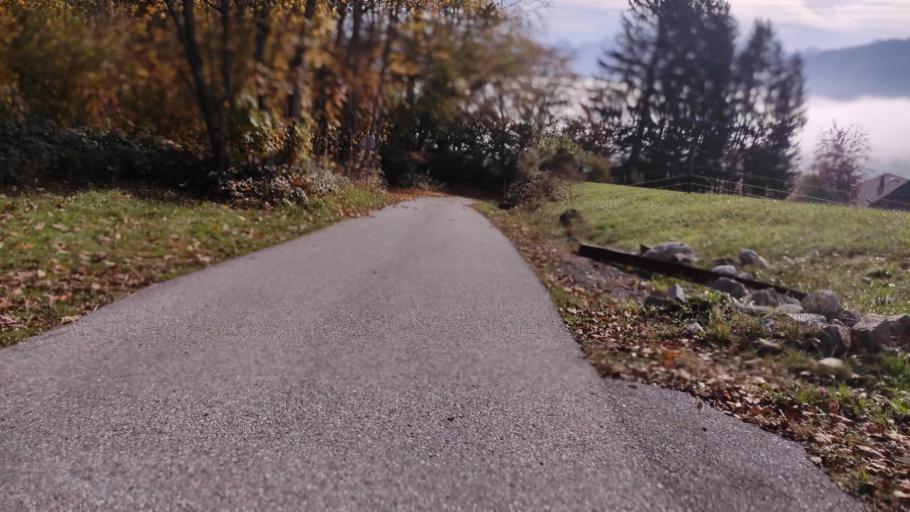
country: AT
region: Salzburg
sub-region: Politischer Bezirk Salzburg-Umgebung
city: Sankt Gilgen
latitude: 47.7765
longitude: 13.3567
